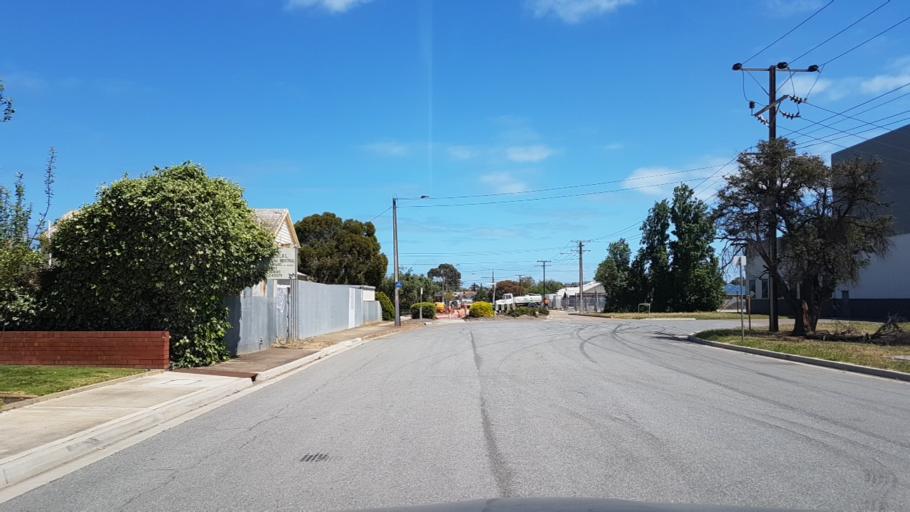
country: AU
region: South Australia
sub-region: Charles Sturt
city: Woodville North
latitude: -34.8631
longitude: 138.5350
